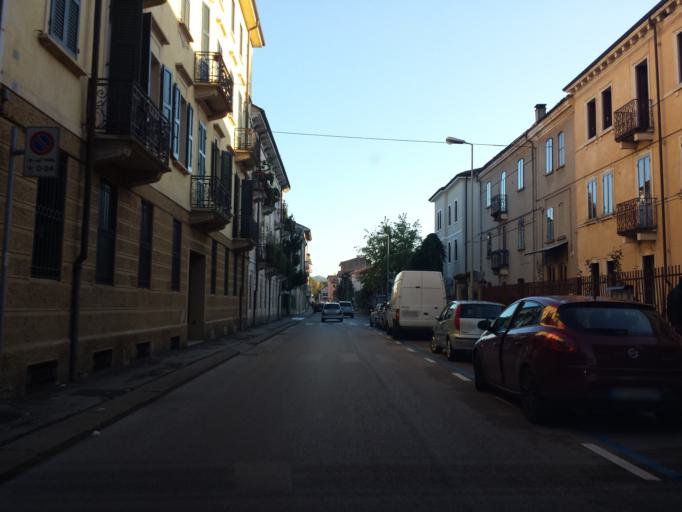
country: IT
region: Veneto
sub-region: Provincia di Vicenza
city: Vicenza
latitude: 45.5456
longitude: 11.5282
